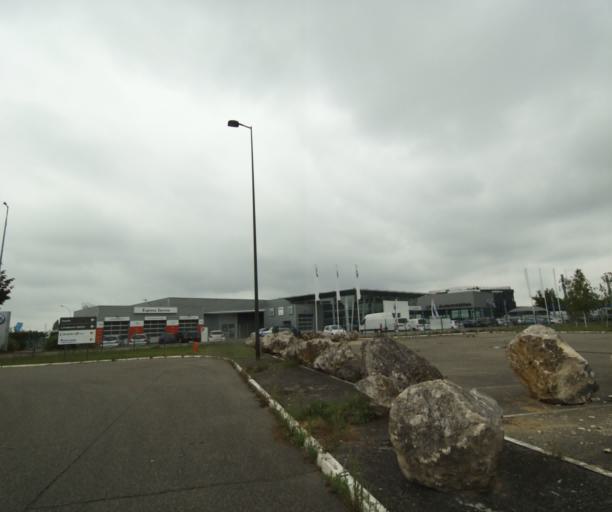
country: FR
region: Midi-Pyrenees
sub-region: Departement du Tarn-et-Garonne
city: Bressols
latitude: 43.9899
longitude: 1.3346
